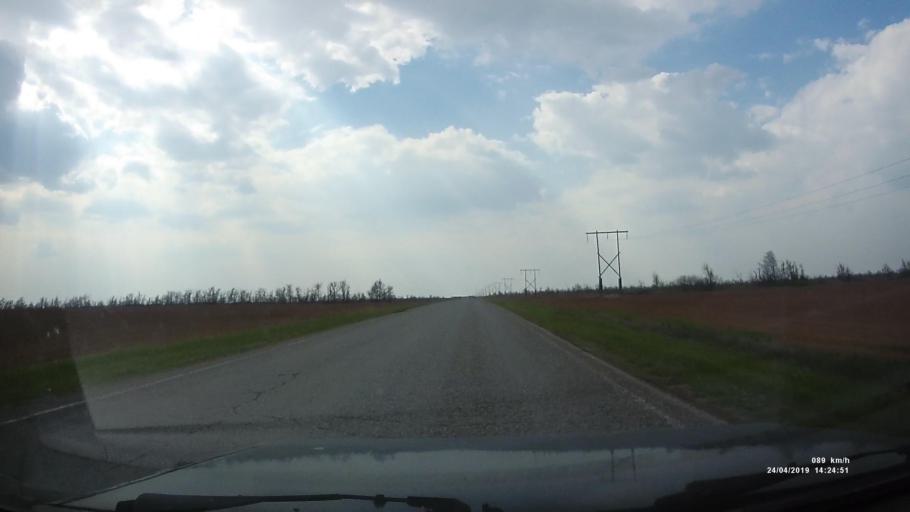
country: RU
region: Kalmykiya
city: Arshan'
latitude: 46.3293
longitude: 44.0895
